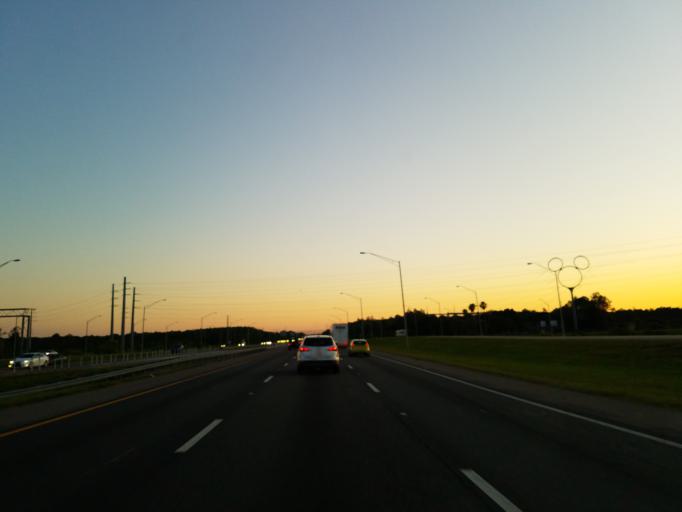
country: US
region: Florida
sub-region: Osceola County
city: Celebration
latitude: 28.3047
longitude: -81.5719
